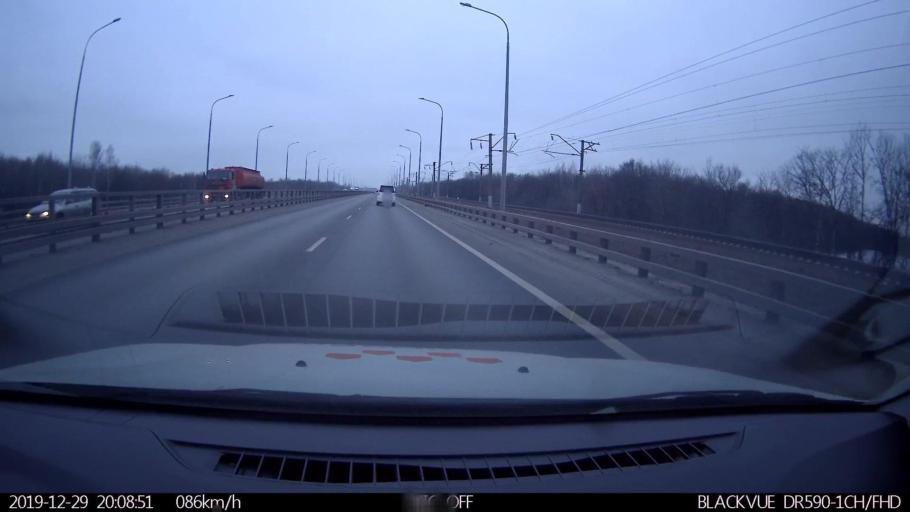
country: RU
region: Nizjnij Novgorod
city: Neklyudovo
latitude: 56.3809
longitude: 43.9586
